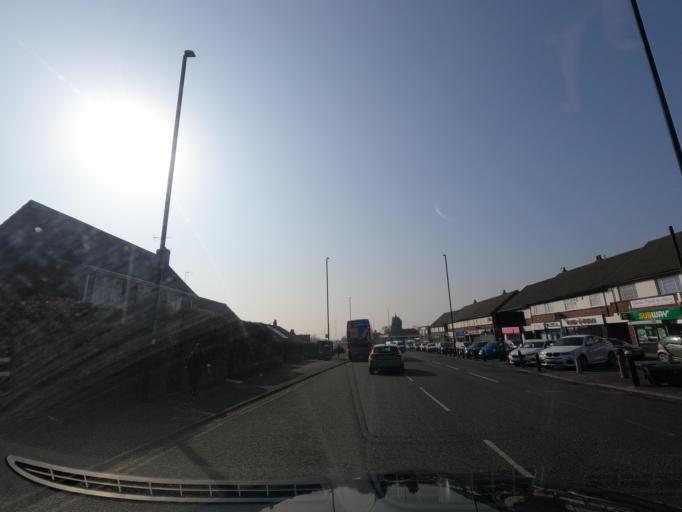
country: GB
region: England
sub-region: Newcastle upon Tyne
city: Gosforth
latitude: 55.0084
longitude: -1.5782
